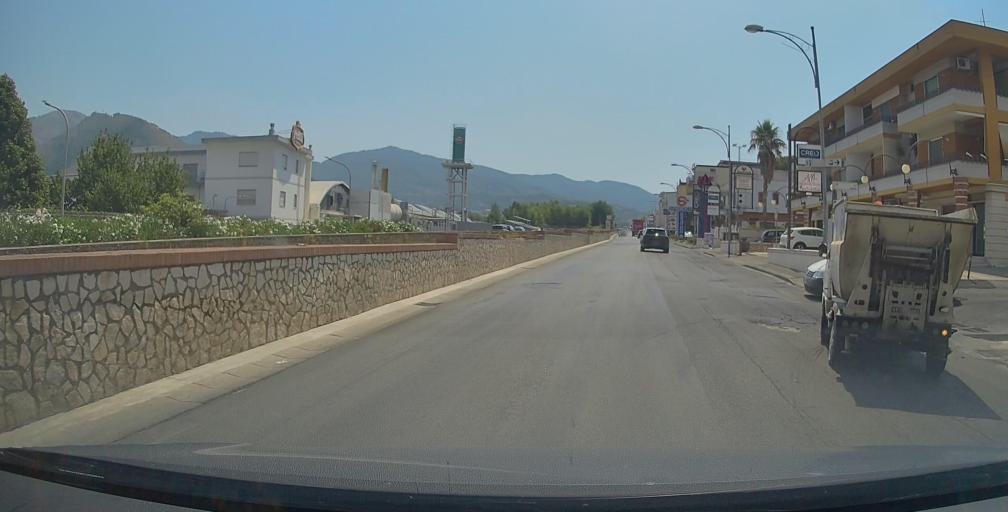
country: IT
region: Campania
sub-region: Provincia di Salerno
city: Nocera Superiore
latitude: 40.7392
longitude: 14.6726
